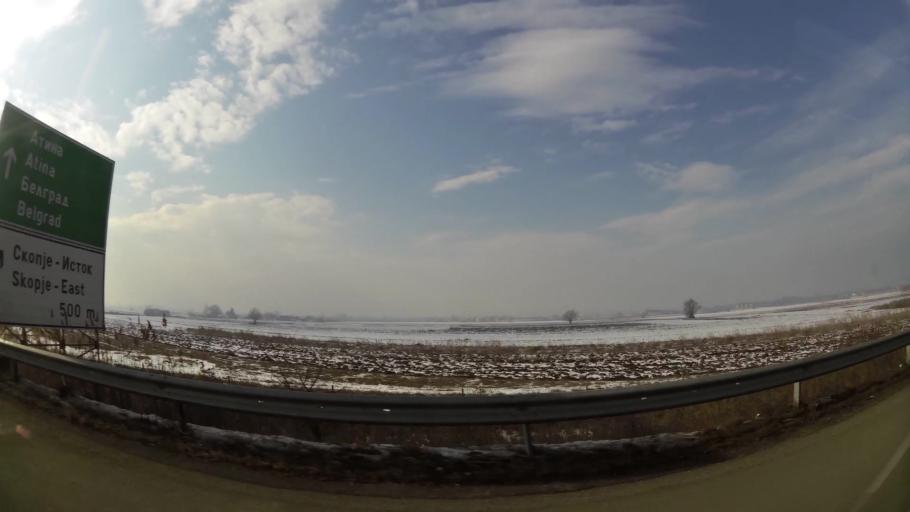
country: MK
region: Aracinovo
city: Arachinovo
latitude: 42.0030
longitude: 21.5341
